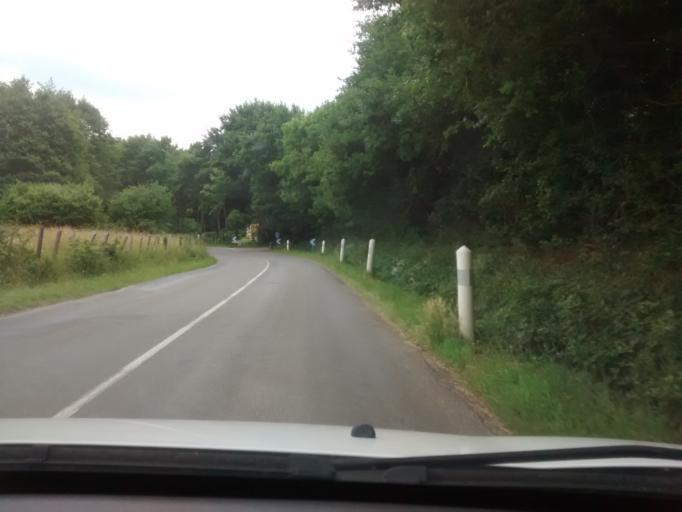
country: FR
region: Brittany
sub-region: Departement d'Ille-et-Vilaine
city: La Bouexiere
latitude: 48.1982
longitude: -1.4699
